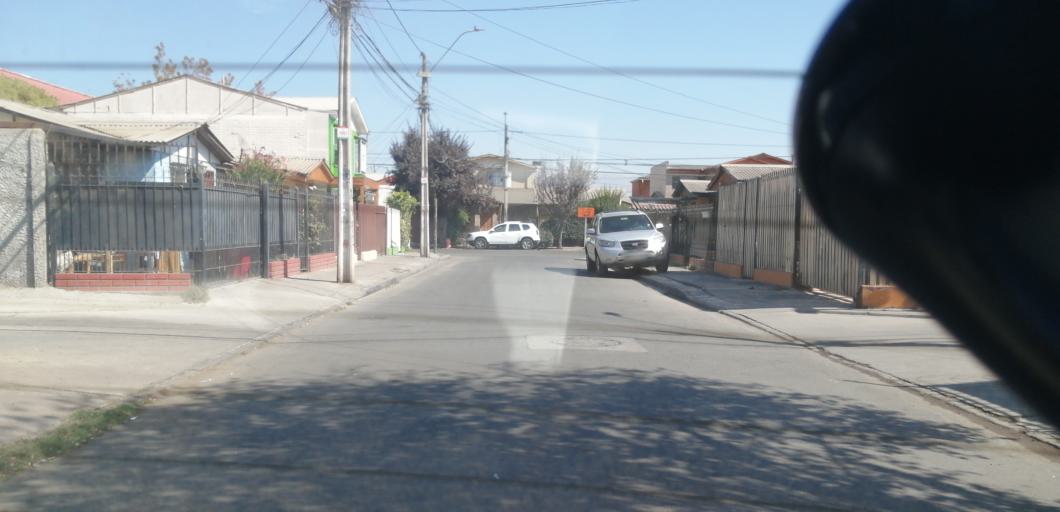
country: CL
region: Santiago Metropolitan
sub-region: Provincia de Santiago
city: Lo Prado
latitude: -33.4645
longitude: -70.7405
